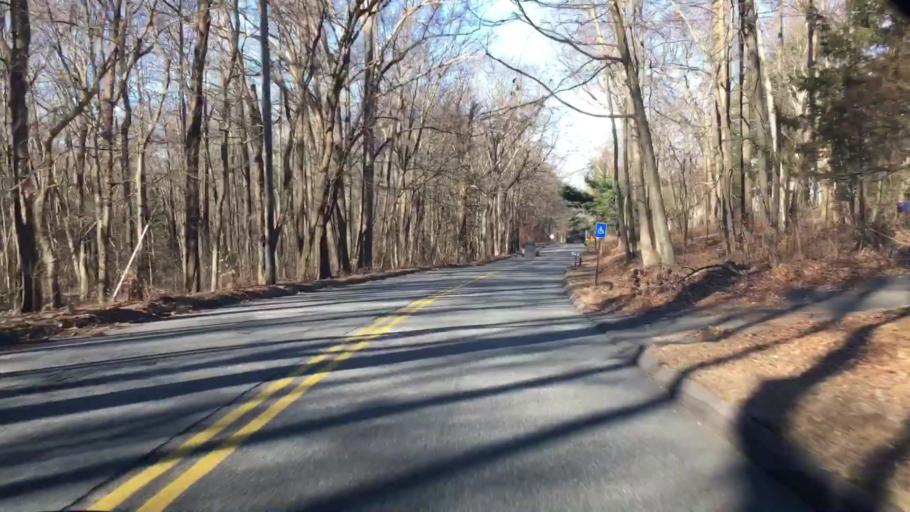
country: US
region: Connecticut
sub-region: Tolland County
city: Tolland
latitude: 41.8947
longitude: -72.3903
